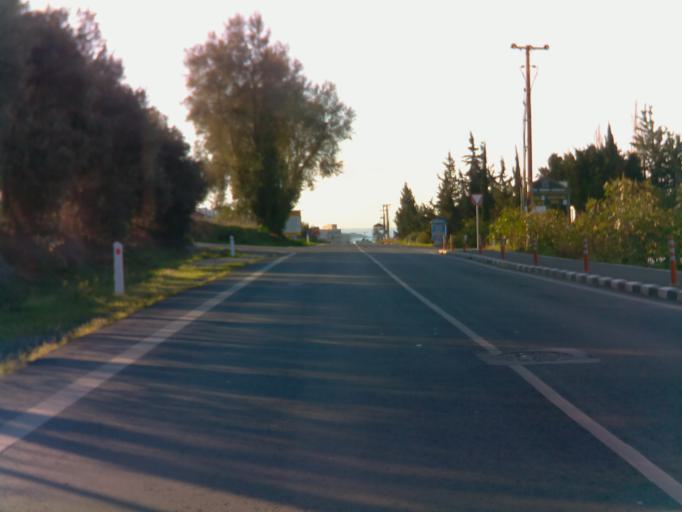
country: CY
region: Pafos
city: Kissonerga
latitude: 34.8279
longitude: 32.3923
